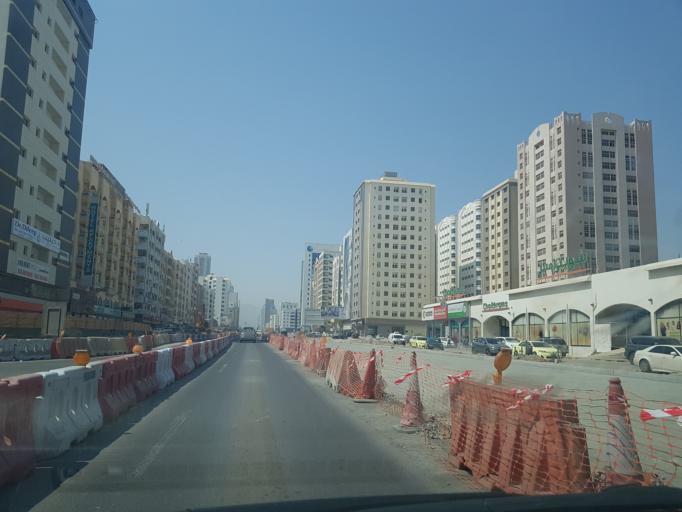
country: AE
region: Al Fujayrah
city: Al Fujayrah
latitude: 25.1219
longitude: 56.3449
